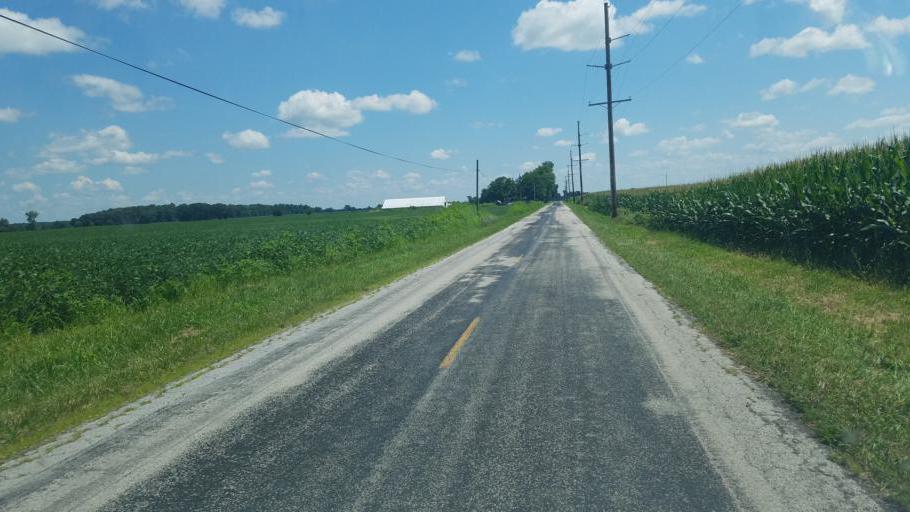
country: US
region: Ohio
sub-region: Marion County
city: Marion
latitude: 40.6297
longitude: -83.2128
